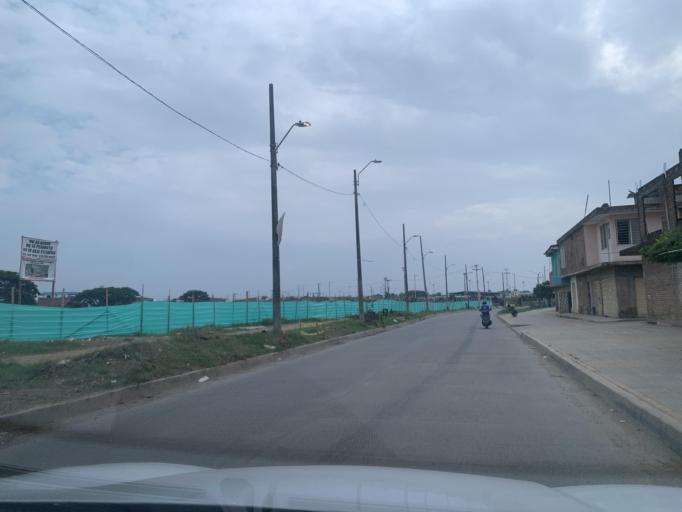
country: CO
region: Valle del Cauca
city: Cali
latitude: 3.4104
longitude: -76.4790
